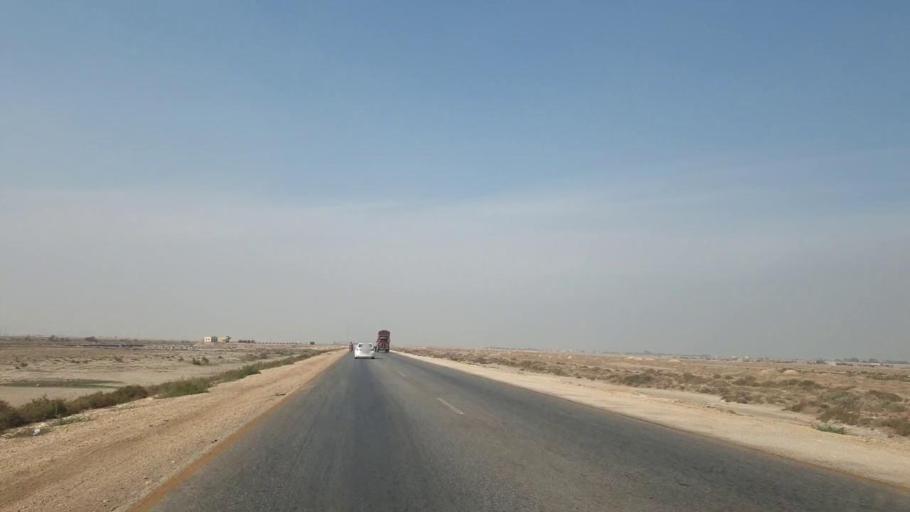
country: PK
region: Sindh
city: Sann
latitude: 25.8865
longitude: 68.2432
